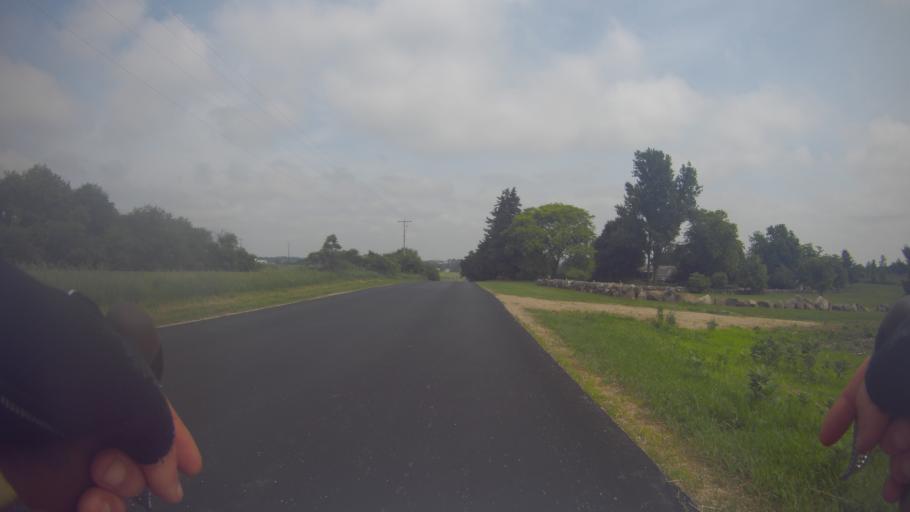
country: US
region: Wisconsin
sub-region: Rock County
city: Edgerton
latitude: 42.9109
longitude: -89.0427
